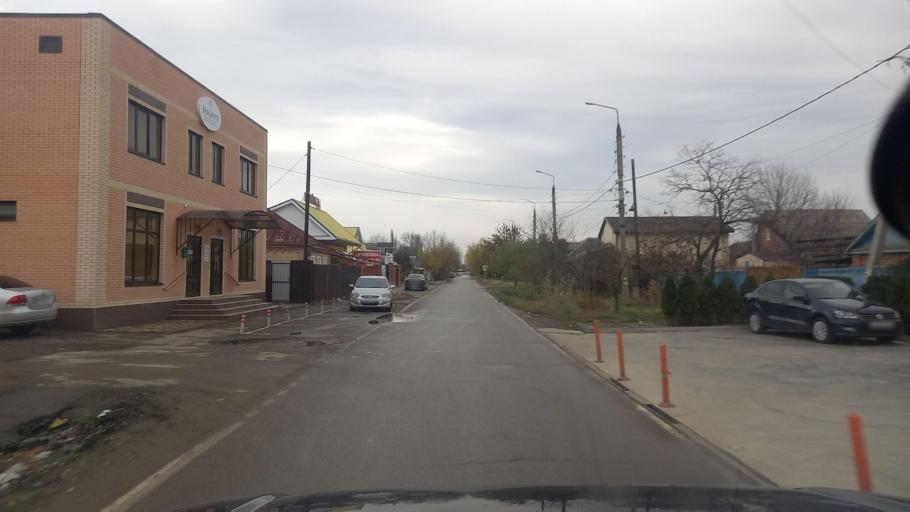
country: RU
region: Adygeya
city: Yablonovskiy
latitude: 44.9798
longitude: 38.9415
